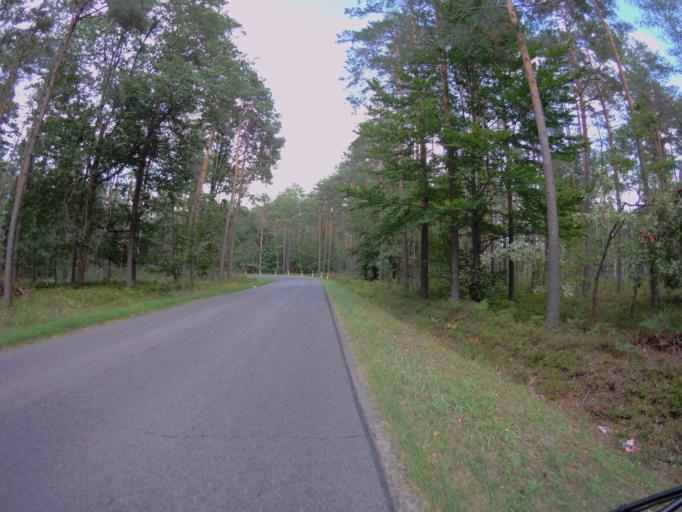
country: PL
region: Subcarpathian Voivodeship
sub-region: Powiat lezajski
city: Brzoza Krolewska
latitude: 50.2453
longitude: 22.3644
